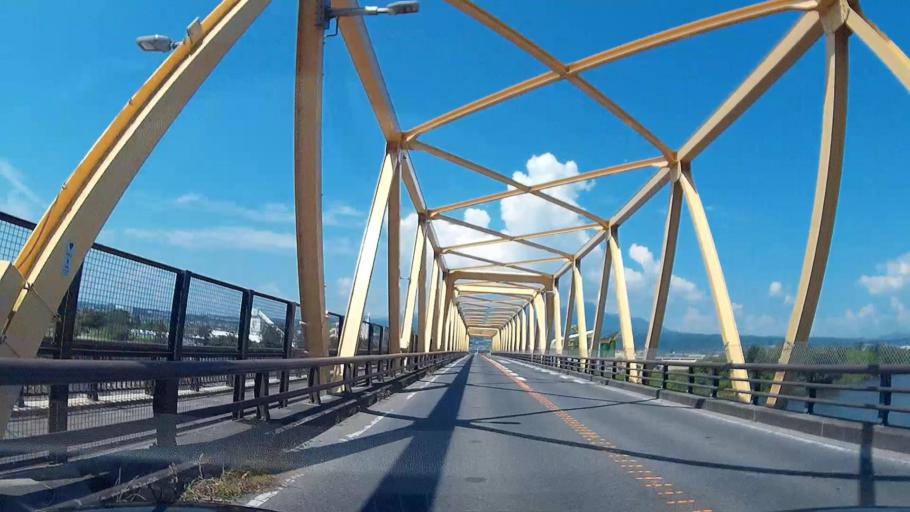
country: JP
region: Gunma
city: Shibukawa
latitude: 36.4643
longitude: 139.0369
